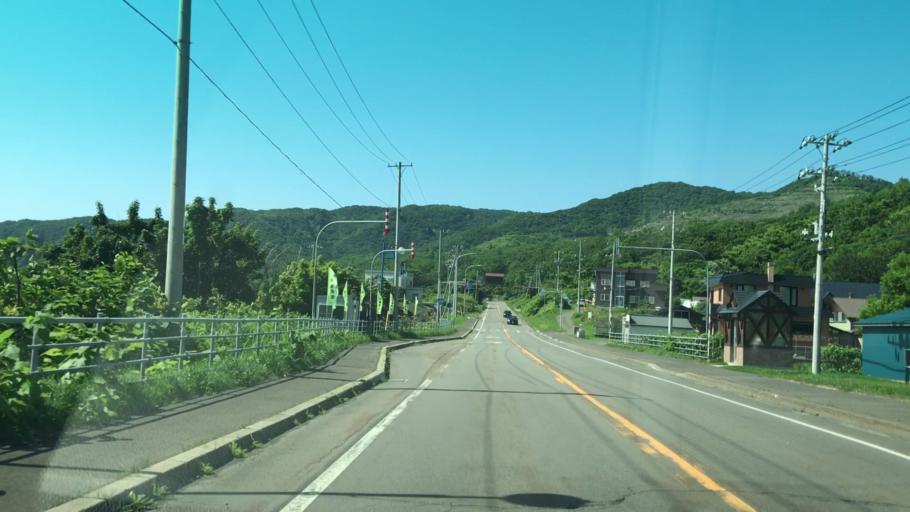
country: JP
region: Hokkaido
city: Iwanai
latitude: 43.0729
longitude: 140.4891
